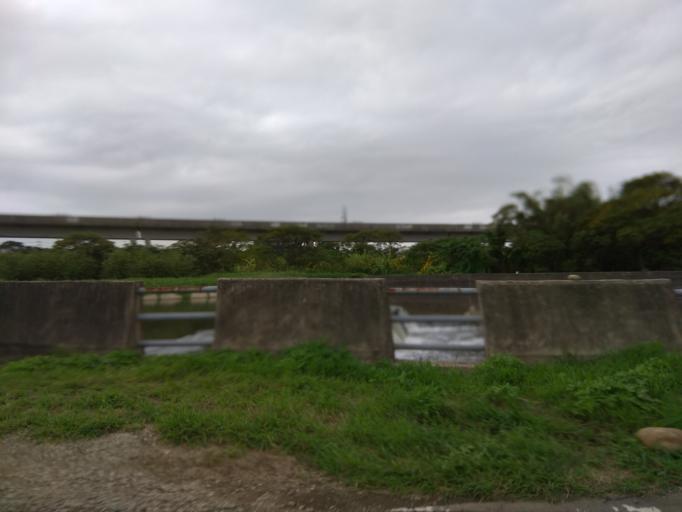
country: TW
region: Taiwan
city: Taoyuan City
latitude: 25.0492
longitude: 121.2139
